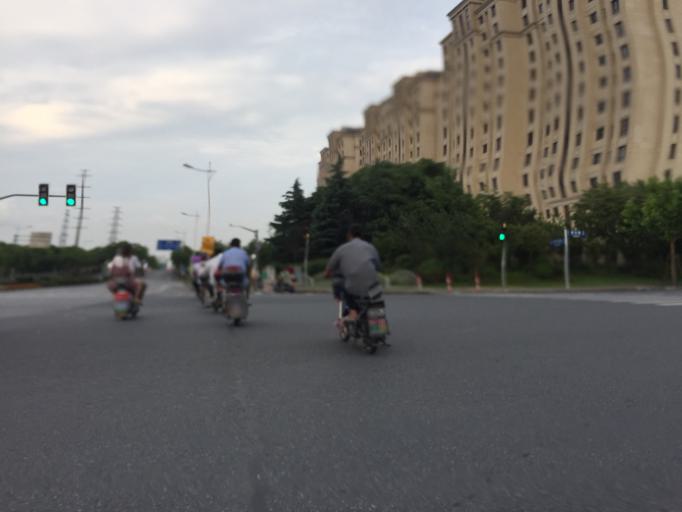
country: CN
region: Shanghai Shi
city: Huamu
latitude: 31.1895
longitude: 121.5415
